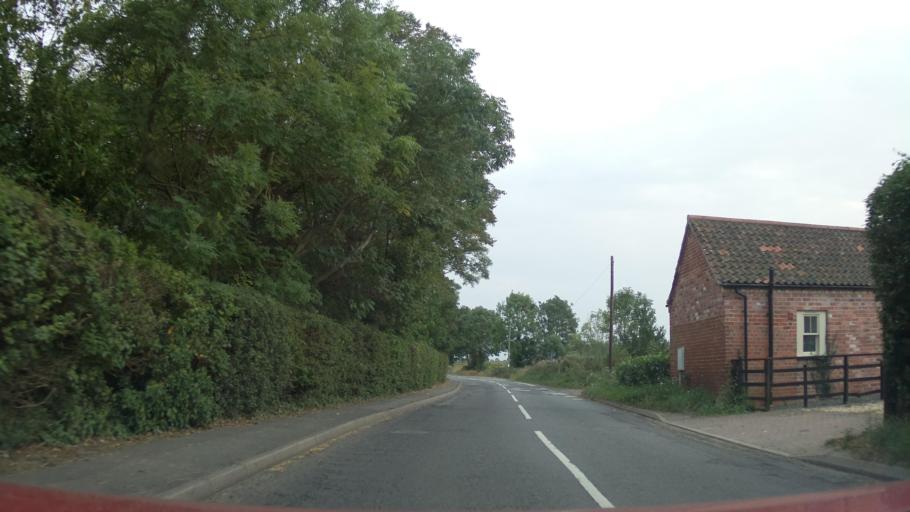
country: GB
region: England
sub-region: Lincolnshire
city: Skellingthorpe
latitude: 53.1423
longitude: -0.6458
